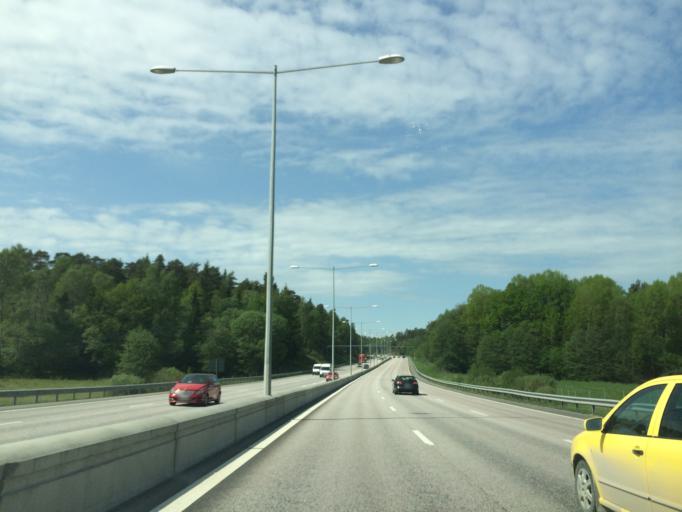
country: SE
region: Stockholm
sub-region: Salems Kommun
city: Ronninge
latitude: 59.2109
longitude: 17.7342
